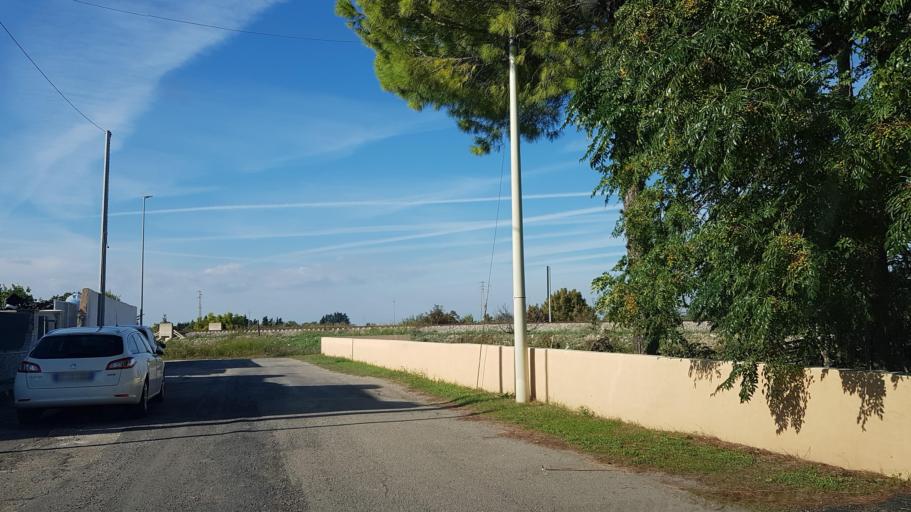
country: IT
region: Apulia
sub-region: Provincia di Lecce
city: Salice Salentino
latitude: 40.3915
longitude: 17.9605
